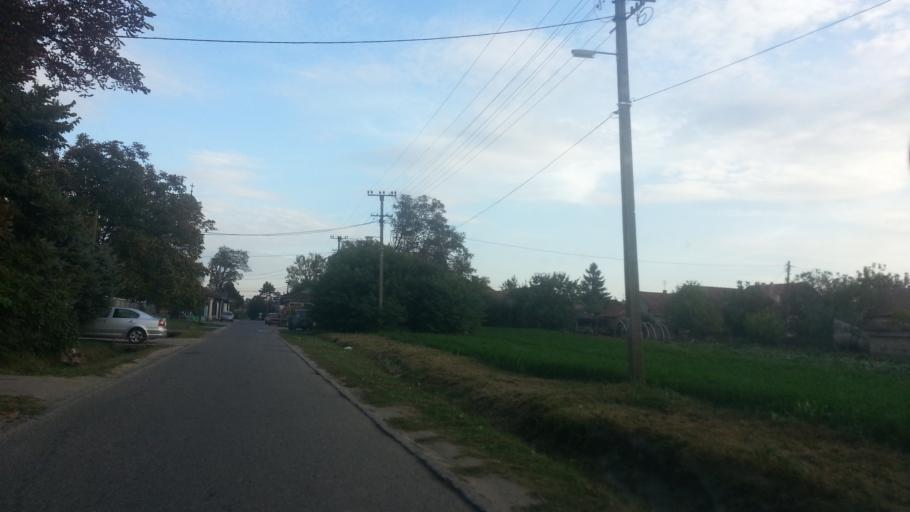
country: RS
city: Belegis
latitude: 45.0204
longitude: 20.3317
